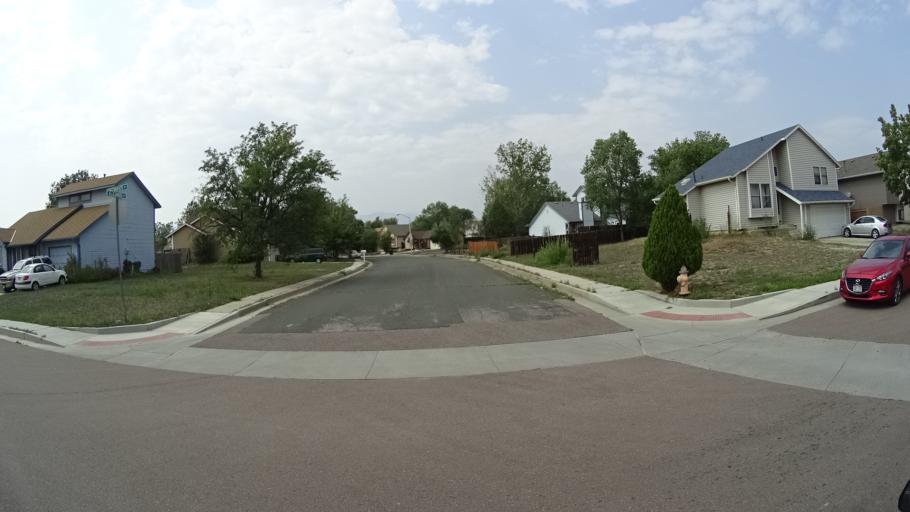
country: US
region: Colorado
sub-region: El Paso County
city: Stratmoor
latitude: 38.8193
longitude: -104.7440
